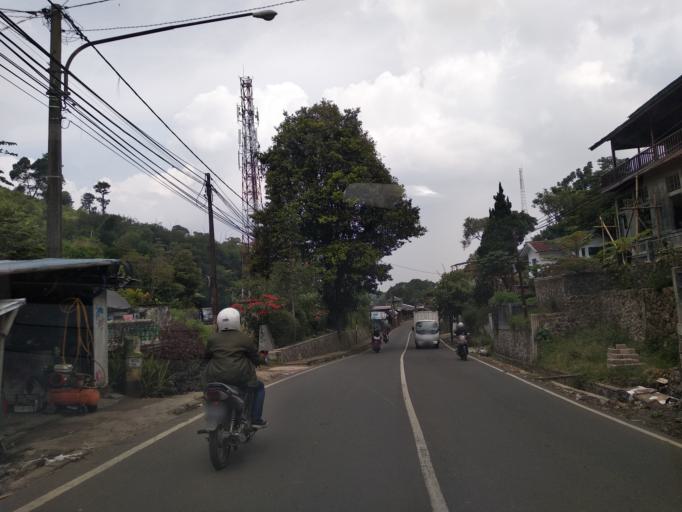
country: ID
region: West Java
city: Lembang
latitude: -6.8242
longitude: 107.6104
